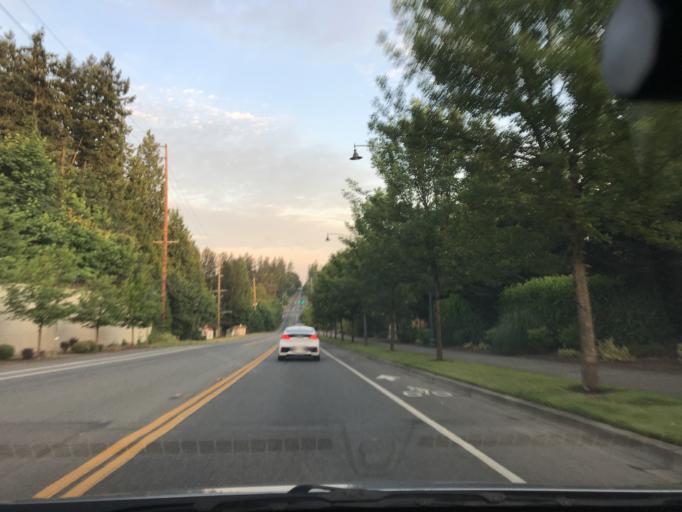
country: US
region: Washington
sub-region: King County
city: Maple Valley
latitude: 47.3580
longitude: -122.0382
